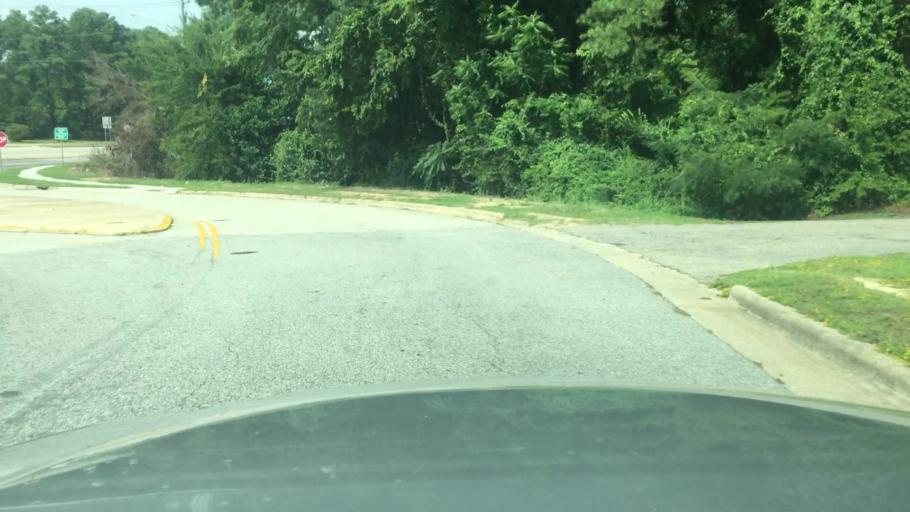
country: US
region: North Carolina
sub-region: Cumberland County
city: Fort Bragg
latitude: 35.0867
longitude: -78.9488
